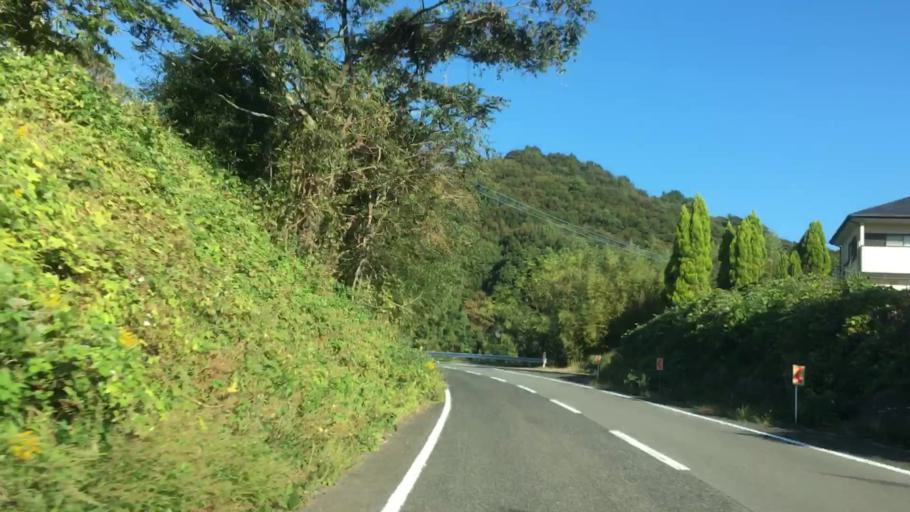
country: JP
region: Nagasaki
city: Sasebo
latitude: 32.9953
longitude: 129.7210
